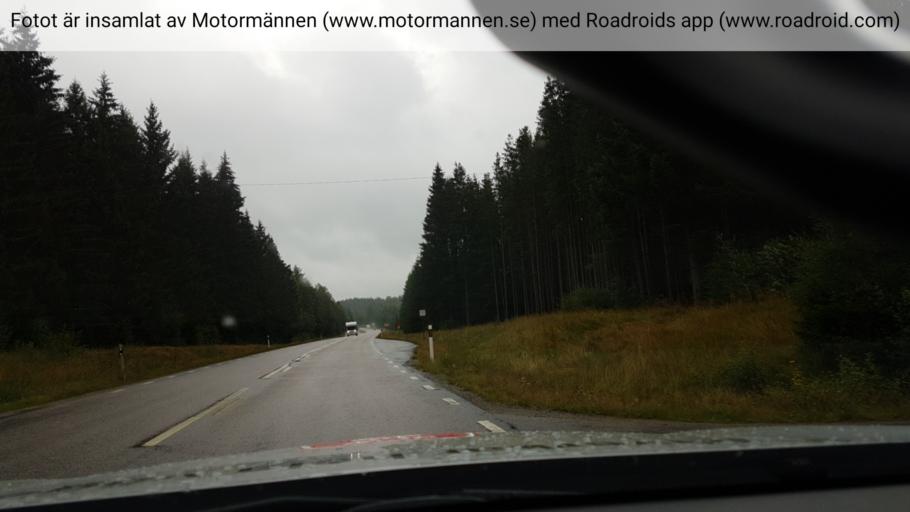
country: SE
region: Vaestra Goetaland
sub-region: Dals-Ed Kommun
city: Ed
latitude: 58.8902
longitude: 11.9201
